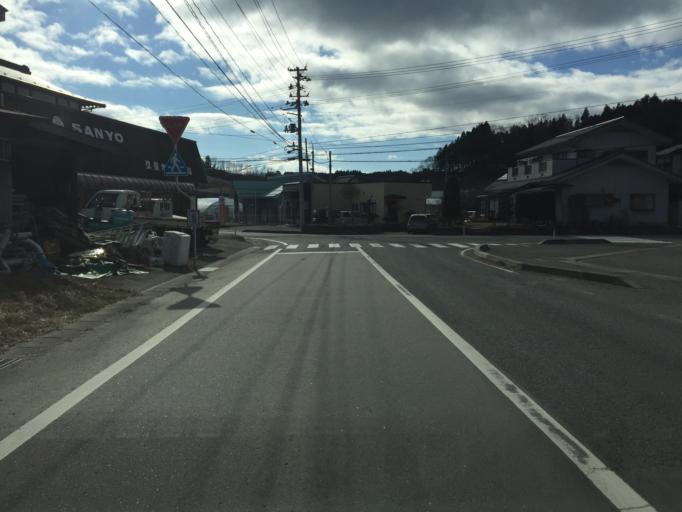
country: JP
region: Fukushima
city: Ishikawa
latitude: 37.2179
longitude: 140.5716
